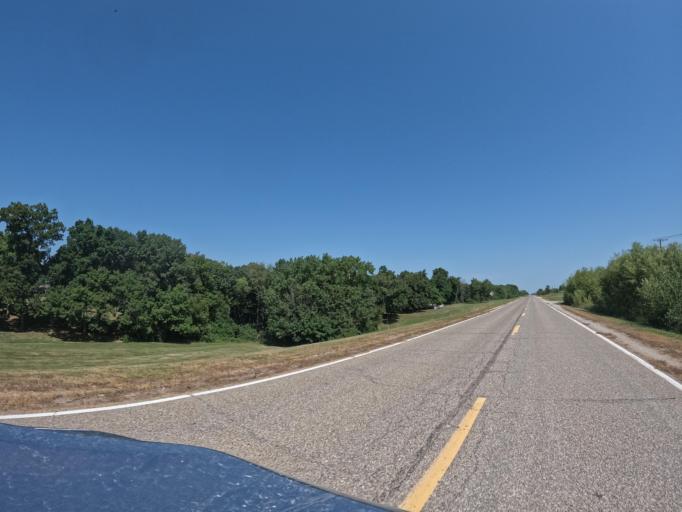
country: US
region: Iowa
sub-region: Henry County
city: Mount Pleasant
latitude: 40.9317
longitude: -91.5402
